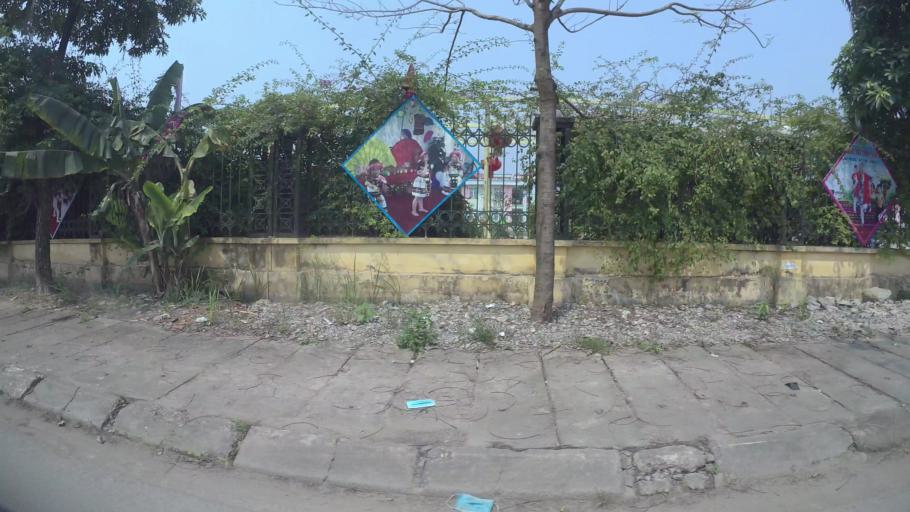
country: VN
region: Ha Noi
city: Ha Dong
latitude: 20.9922
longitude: 105.7683
